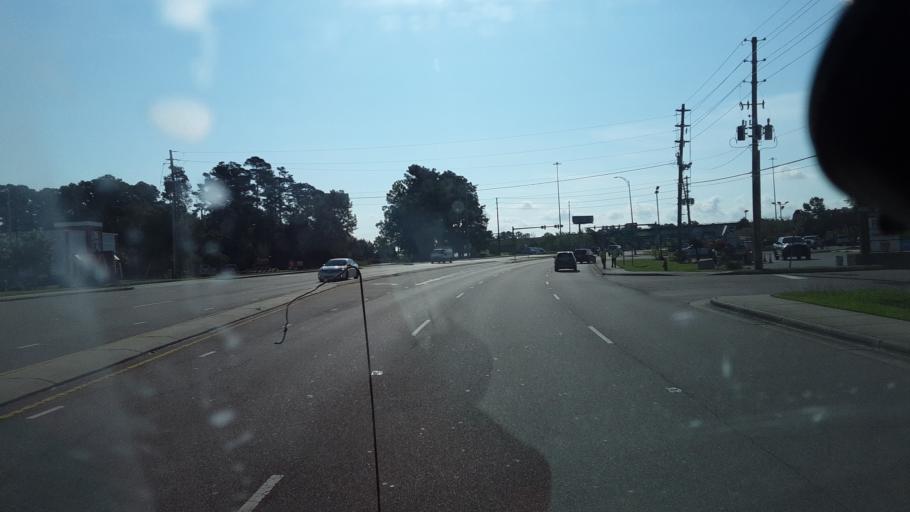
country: US
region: North Carolina
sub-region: Brunswick County
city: Navassa
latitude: 34.2336
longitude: -77.9970
